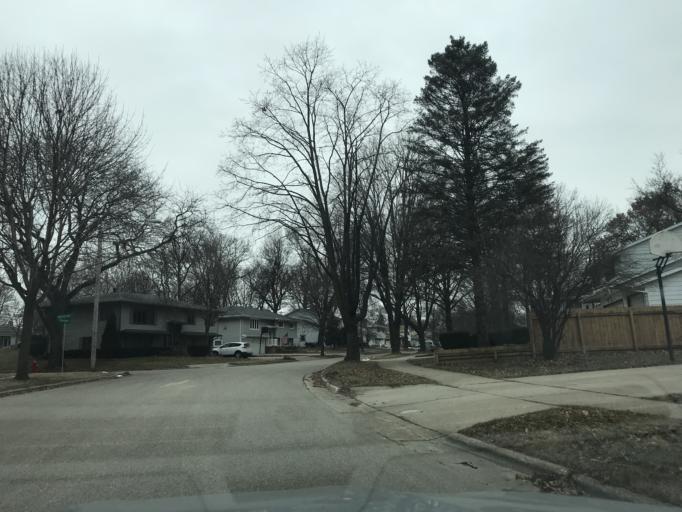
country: US
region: Wisconsin
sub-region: Dane County
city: Monona
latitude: 43.0898
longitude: -89.2996
